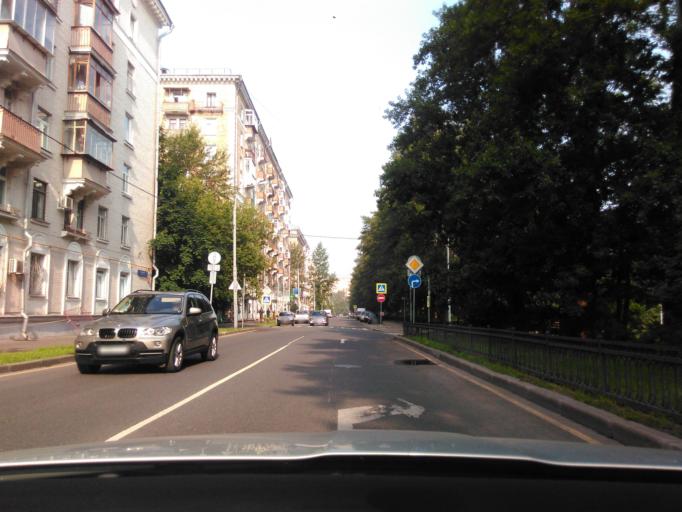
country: RU
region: Moscow
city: Sokol
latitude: 55.7946
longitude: 37.5185
